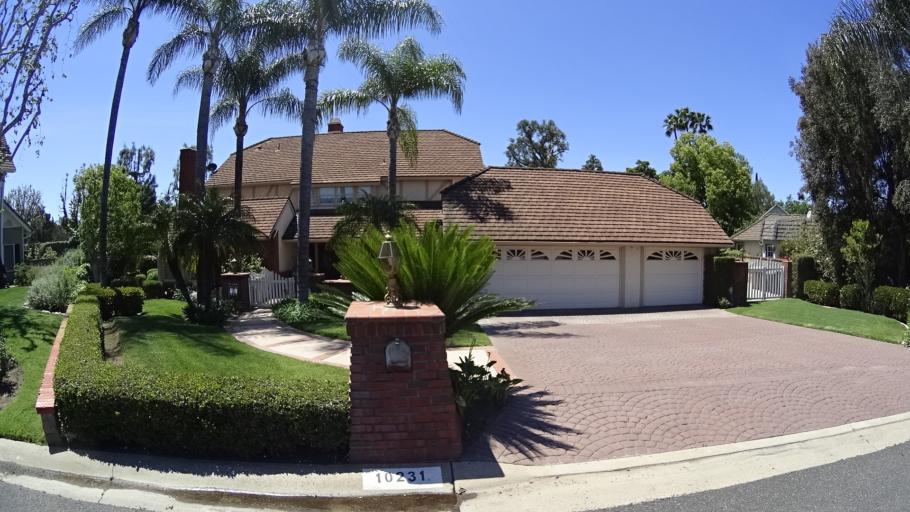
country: US
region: California
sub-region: Orange County
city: Villa Park
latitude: 33.8137
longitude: -117.8146
